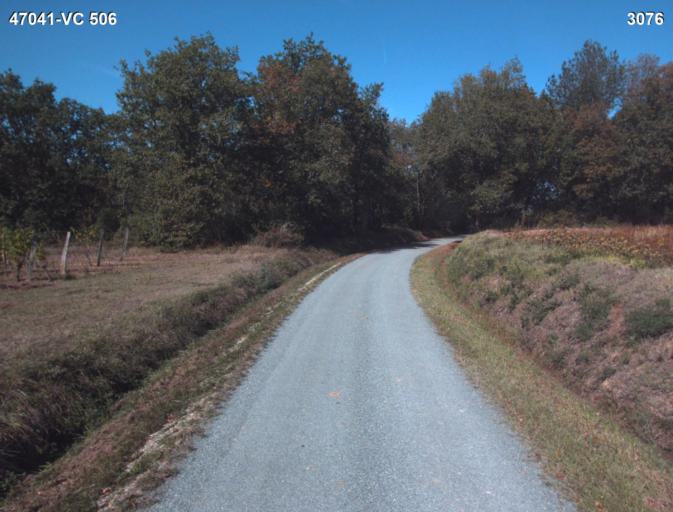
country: FR
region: Aquitaine
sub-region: Departement du Lot-et-Garonne
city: Vianne
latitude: 44.1910
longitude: 0.3813
